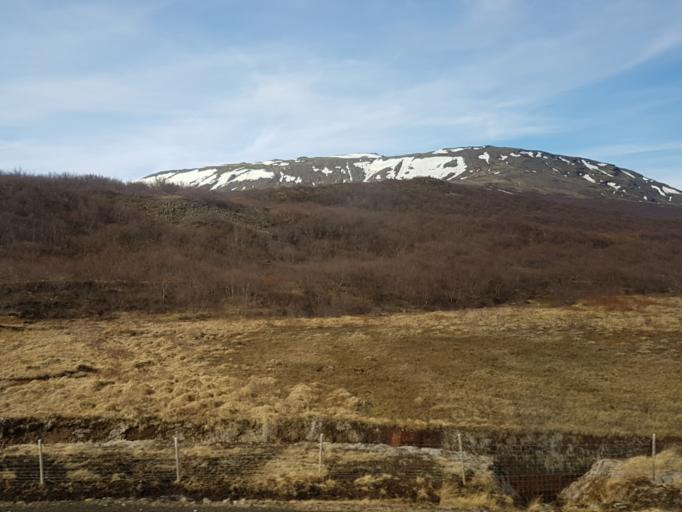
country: IS
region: South
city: Selfoss
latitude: 64.2259
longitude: -20.6006
